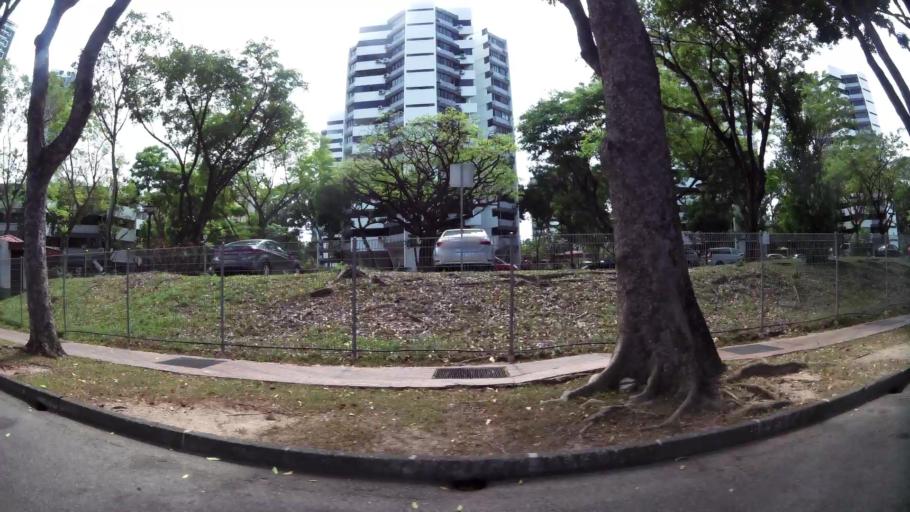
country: SG
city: Singapore
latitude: 1.3176
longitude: 103.7591
